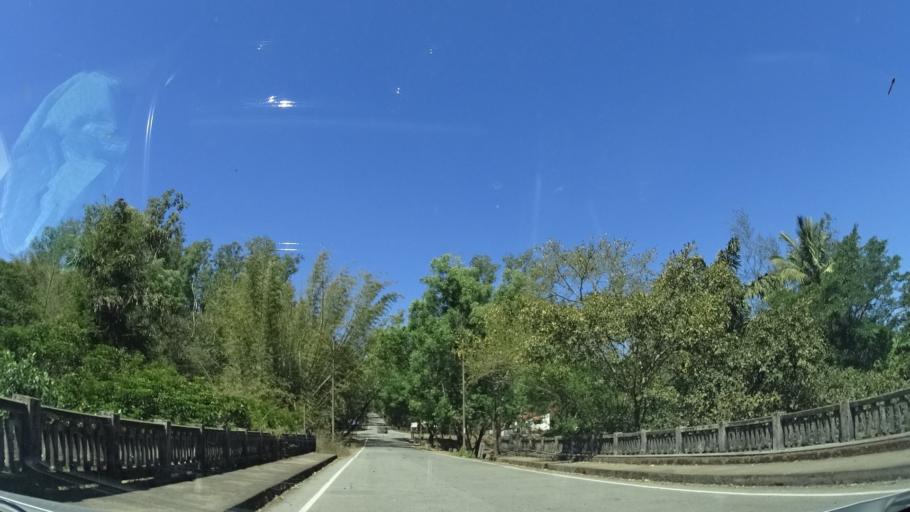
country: IN
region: Karnataka
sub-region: Chikmagalur
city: Sringeri
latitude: 13.2134
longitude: 75.2537
